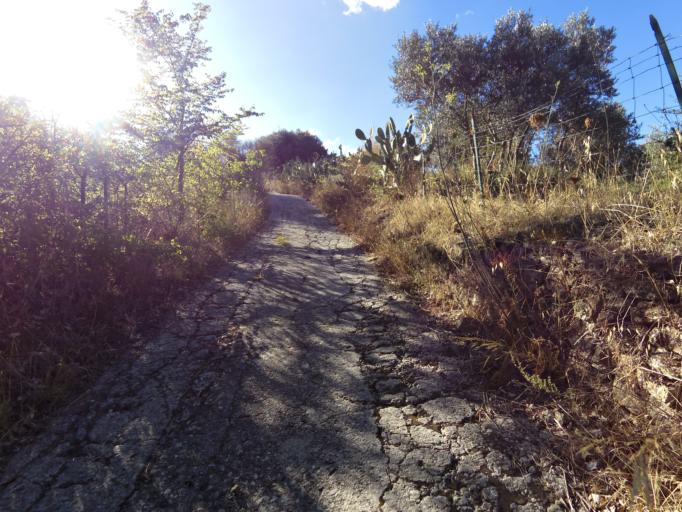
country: IT
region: Calabria
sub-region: Provincia di Reggio Calabria
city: Pazzano
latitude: 38.4480
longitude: 16.4565
